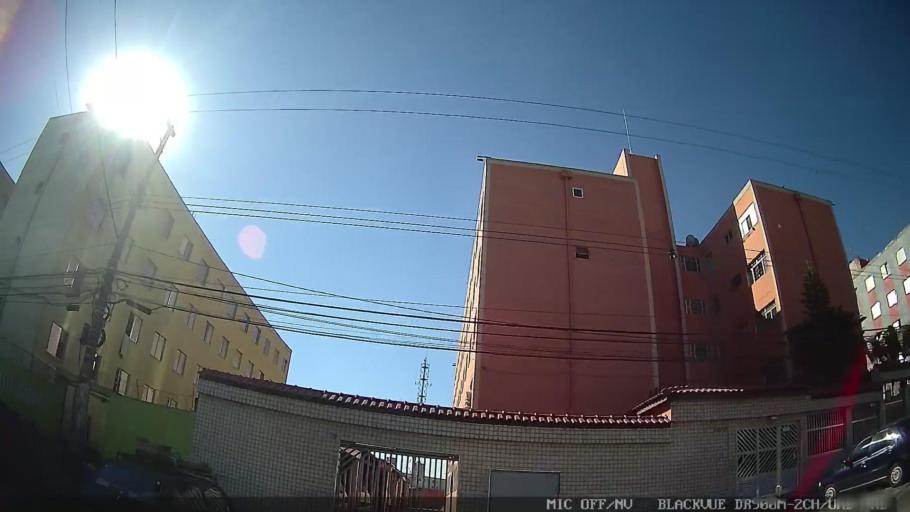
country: BR
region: Sao Paulo
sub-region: Sao Caetano Do Sul
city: Sao Caetano do Sul
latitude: -23.5512
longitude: -46.4823
